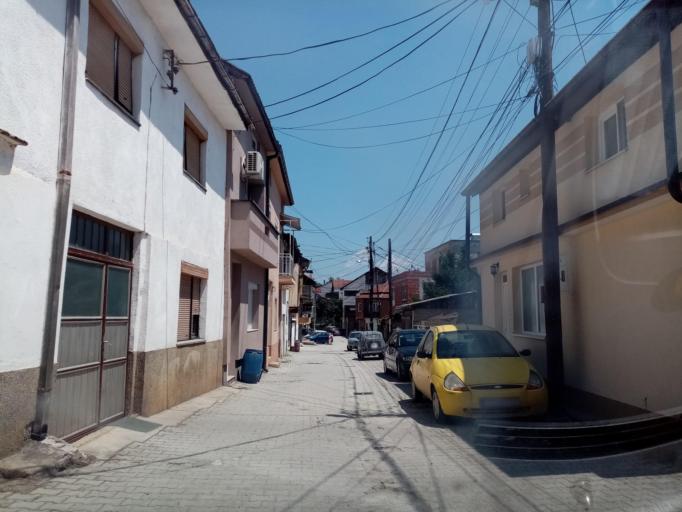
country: MK
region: Tetovo
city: Tetovo
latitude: 42.0148
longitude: 20.9694
